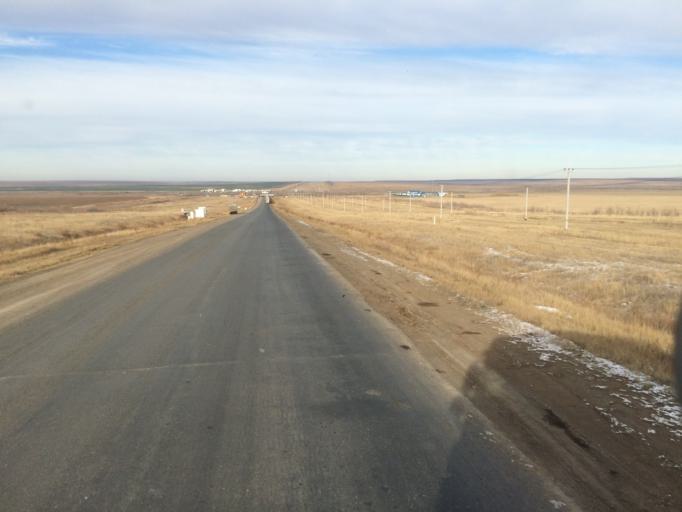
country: KZ
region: Batys Qazaqstan
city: Peremetnoe
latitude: 51.6557
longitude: 51.0096
